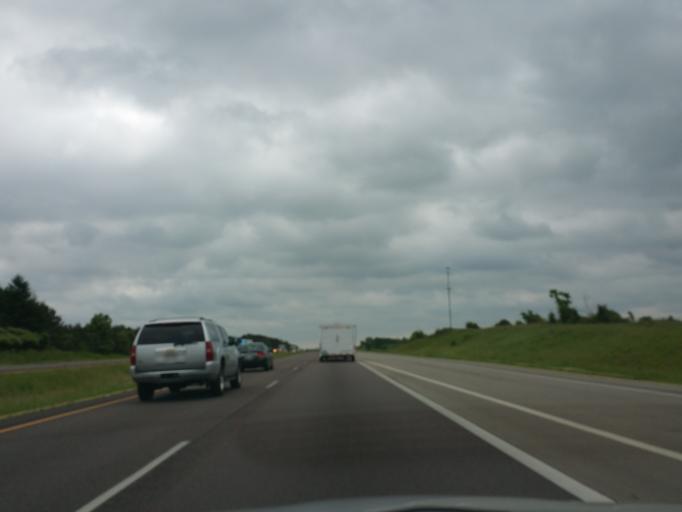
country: US
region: Wisconsin
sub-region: Pierce County
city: Spring Valley
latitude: 44.9333
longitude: -92.1927
